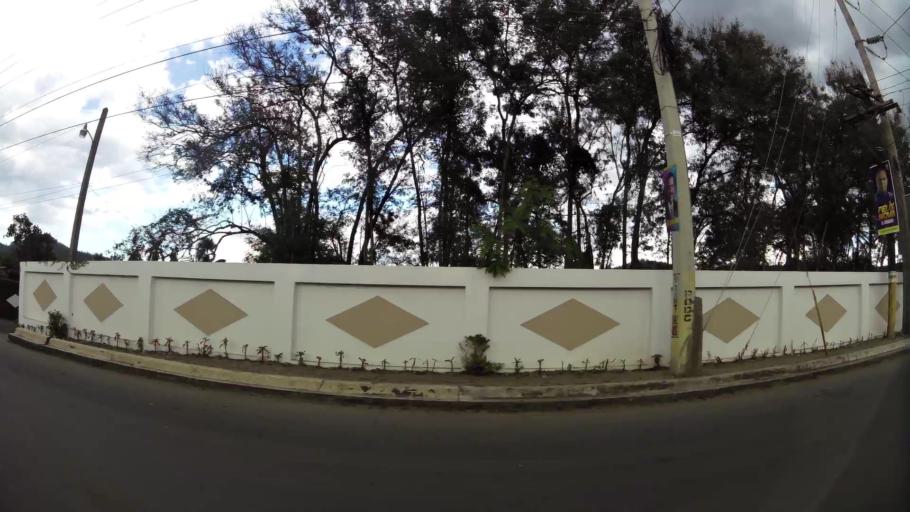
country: DO
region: Monsenor Nouel
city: Bonao
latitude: 18.9521
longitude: -70.4023
